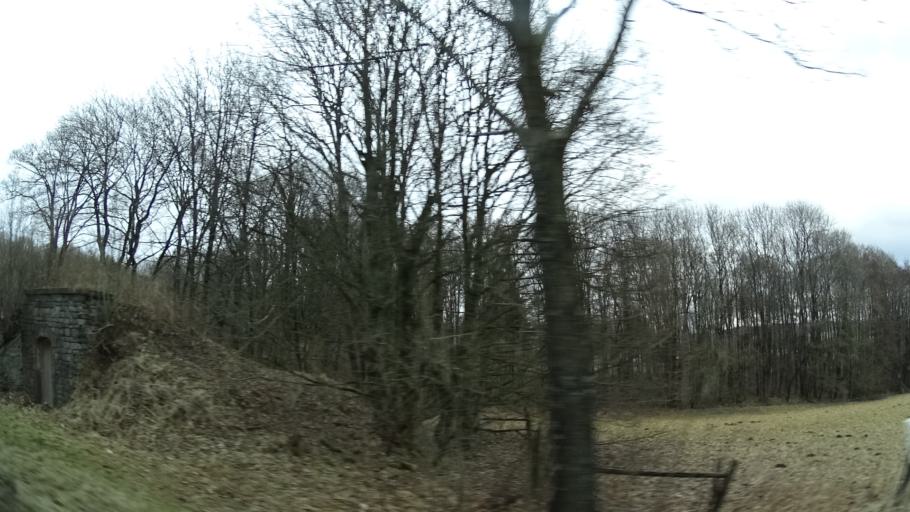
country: DE
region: Hesse
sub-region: Regierungsbezirk Giessen
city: Grebenhain
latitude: 50.4824
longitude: 9.3096
